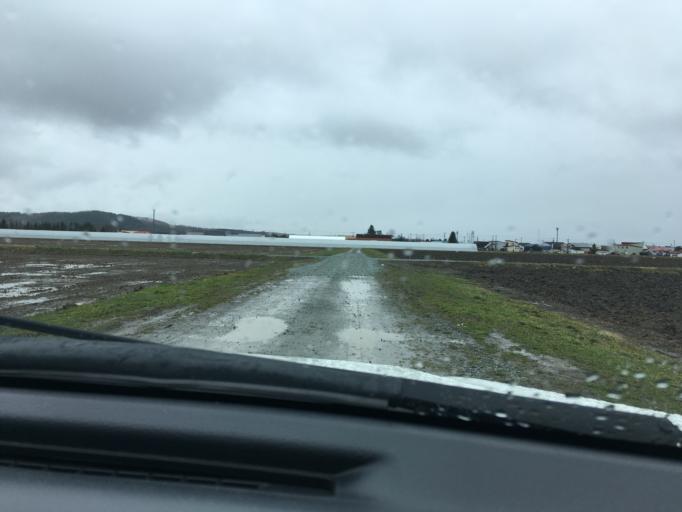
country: JP
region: Hokkaido
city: Nayoro
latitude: 44.1325
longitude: 142.4911
